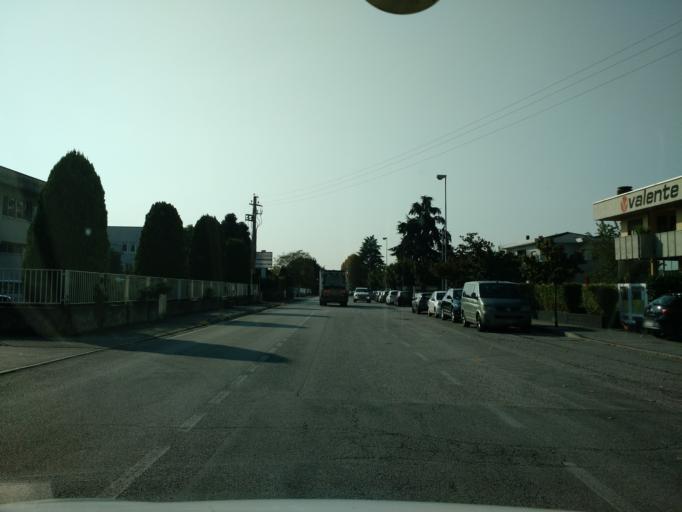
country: IT
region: Veneto
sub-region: Provincia di Vicenza
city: Thiene
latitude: 45.6818
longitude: 11.4680
